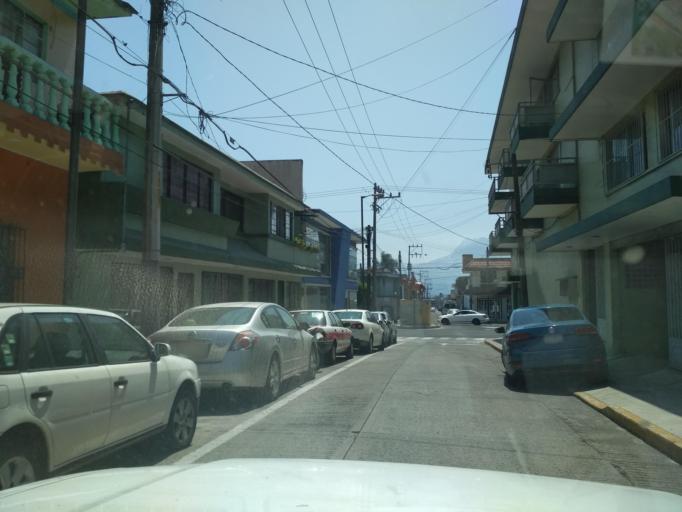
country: MX
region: Veracruz
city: Orizaba
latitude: 18.8502
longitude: -97.0879
